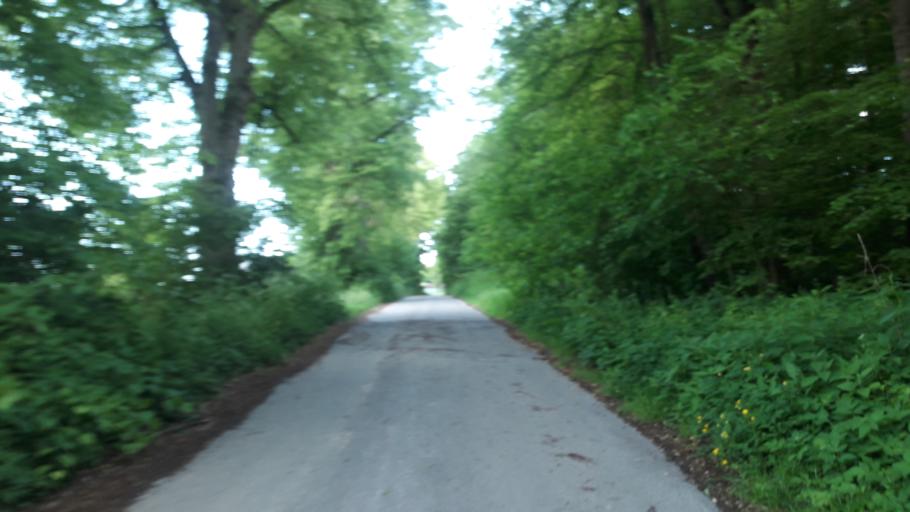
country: DE
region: North Rhine-Westphalia
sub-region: Regierungsbezirk Detmold
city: Paderborn
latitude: 51.6713
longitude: 8.7849
